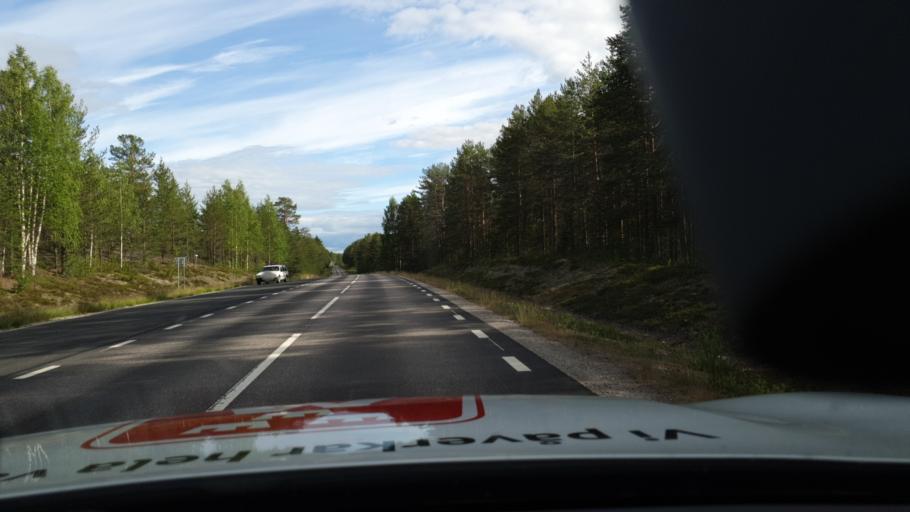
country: SE
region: Norrbotten
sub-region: Overkalix Kommun
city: OEverkalix
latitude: 66.4427
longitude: 22.7870
